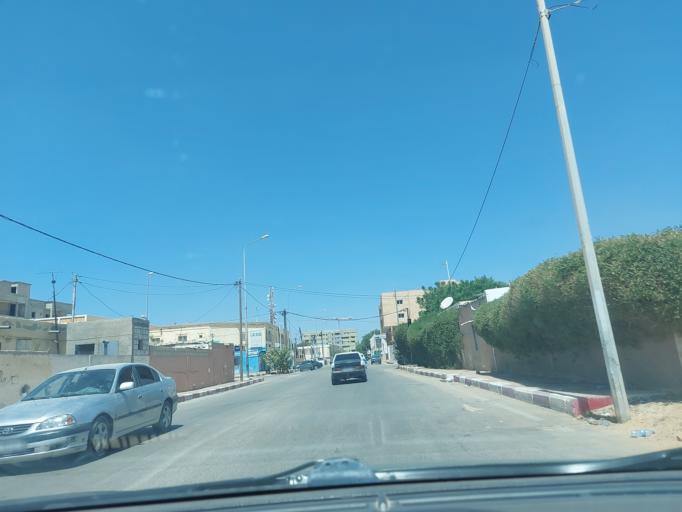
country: MR
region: Nouakchott
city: Nouakchott
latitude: 18.0925
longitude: -15.9755
